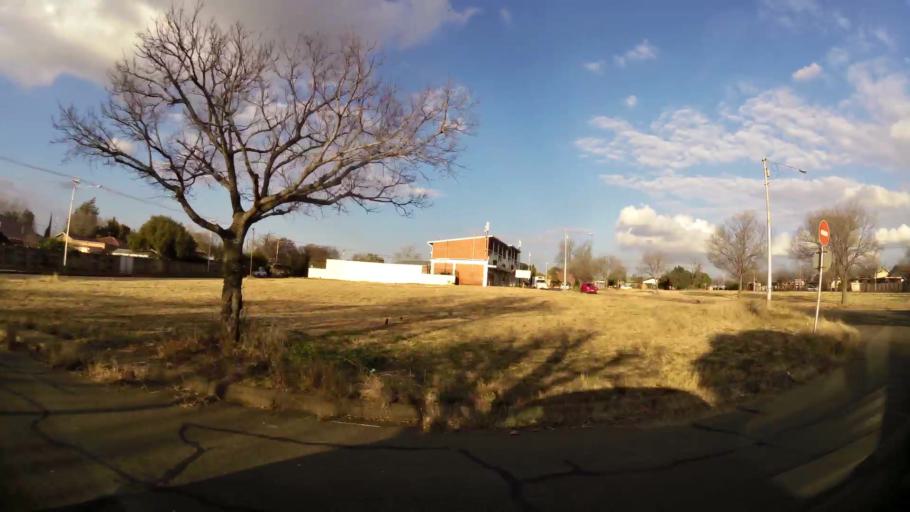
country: ZA
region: Orange Free State
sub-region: Mangaung Metropolitan Municipality
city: Bloemfontein
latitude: -29.1443
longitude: 26.1921
